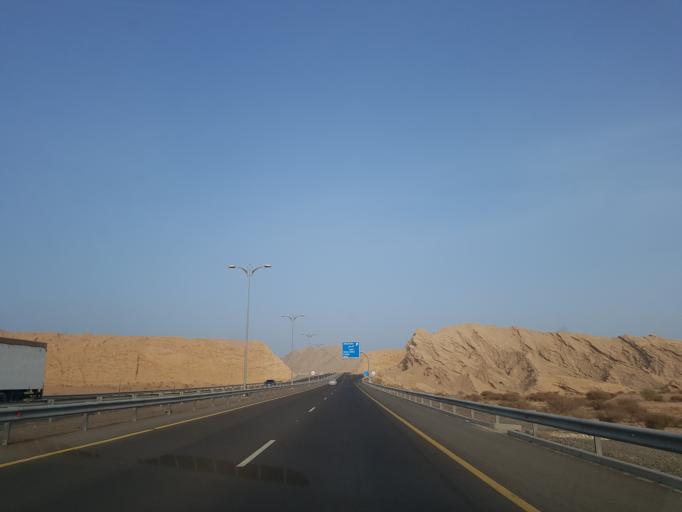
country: OM
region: Al Buraimi
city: Al Buraymi
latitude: 24.2331
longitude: 55.9443
